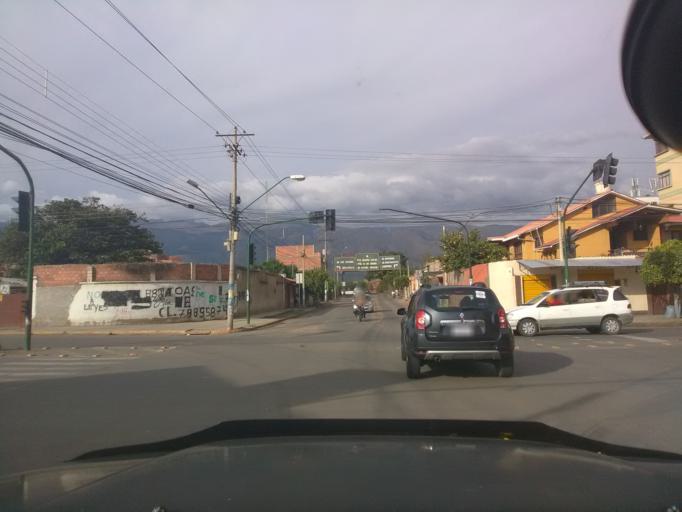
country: BO
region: Cochabamba
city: Cochabamba
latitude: -17.4080
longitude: -66.1710
